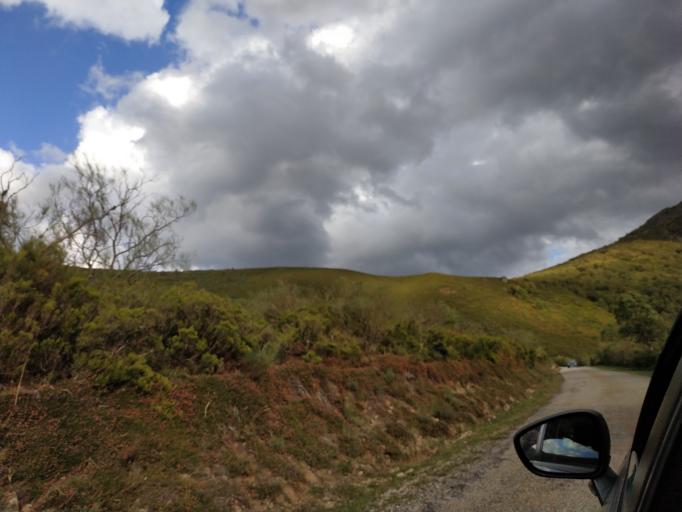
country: ES
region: Castille and Leon
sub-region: Provincia de Leon
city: Candin
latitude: 42.8679
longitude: -6.8367
